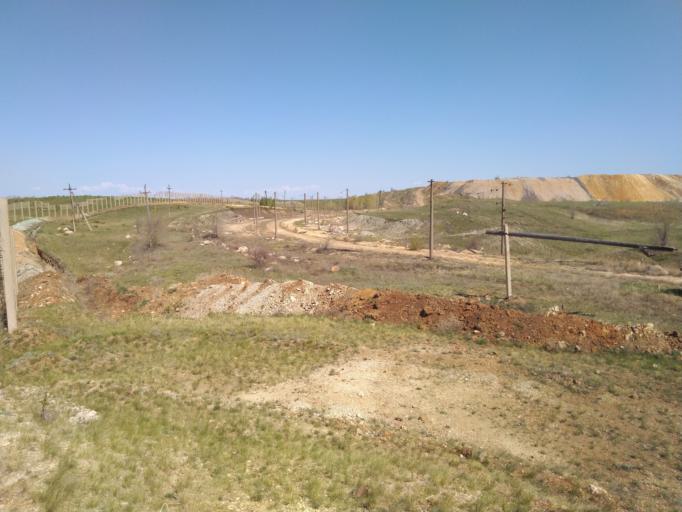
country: RU
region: Orenburg
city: Staraya Akkermanovka
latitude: 51.2127
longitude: 58.1984
